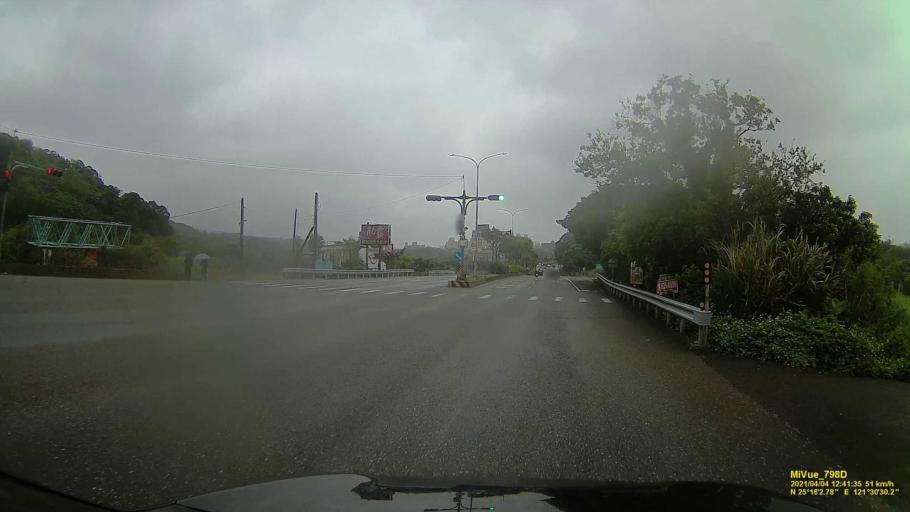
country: TW
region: Taipei
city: Taipei
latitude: 25.2671
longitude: 121.5083
